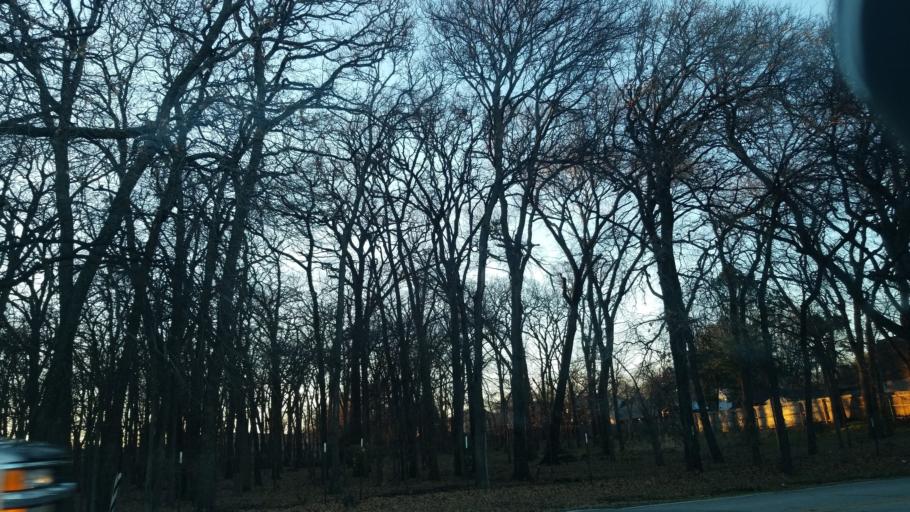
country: US
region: Texas
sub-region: Denton County
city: Hickory Creek
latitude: 33.1355
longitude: -97.0560
